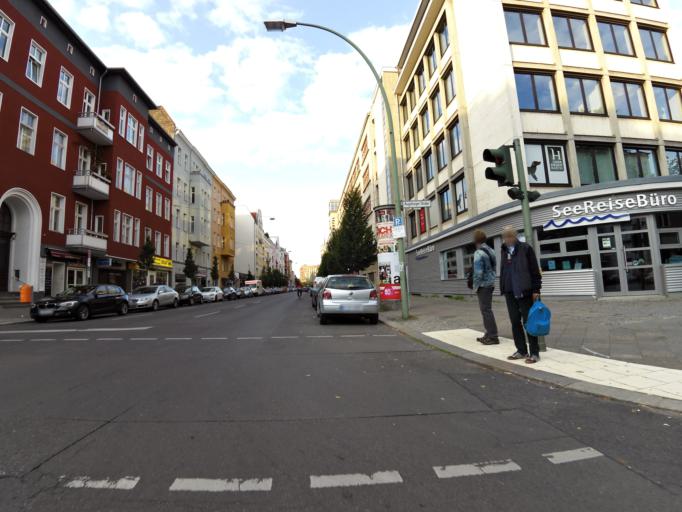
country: DE
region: Berlin
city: Hansaviertel
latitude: 52.5009
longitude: 13.3370
